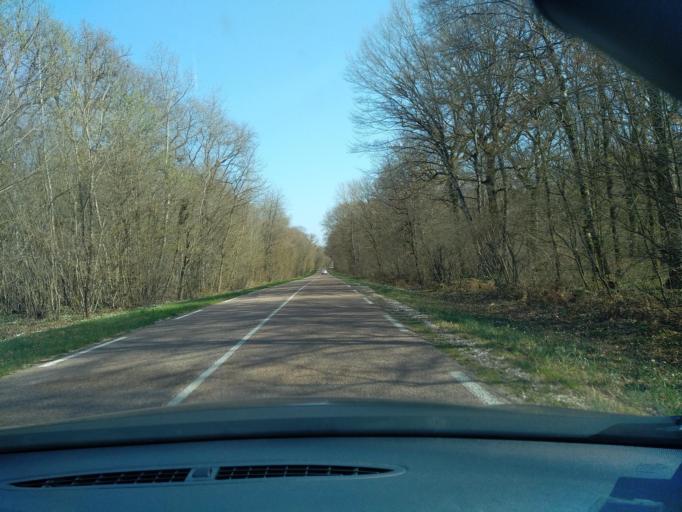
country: FR
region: Franche-Comte
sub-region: Departement du Jura
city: Mont-sous-Vaudrey
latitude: 46.9553
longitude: 5.5275
